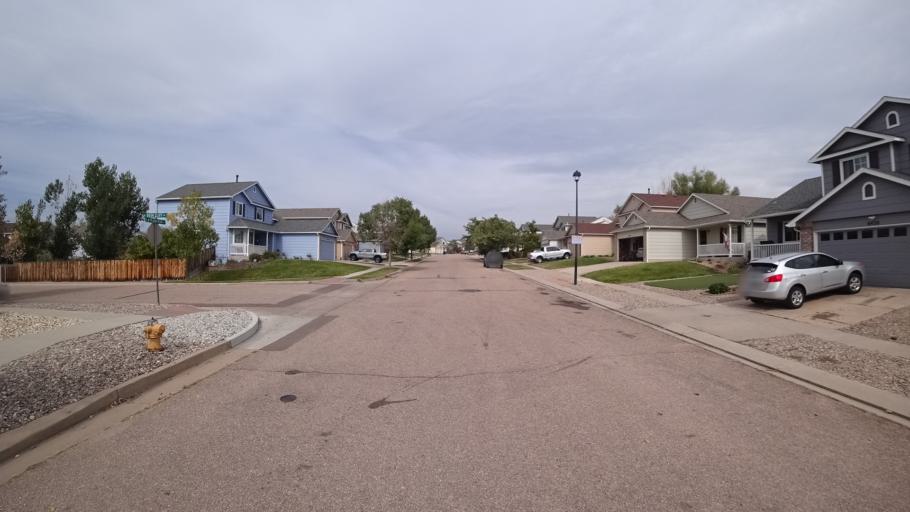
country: US
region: Colorado
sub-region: El Paso County
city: Cimarron Hills
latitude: 38.9147
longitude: -104.7130
